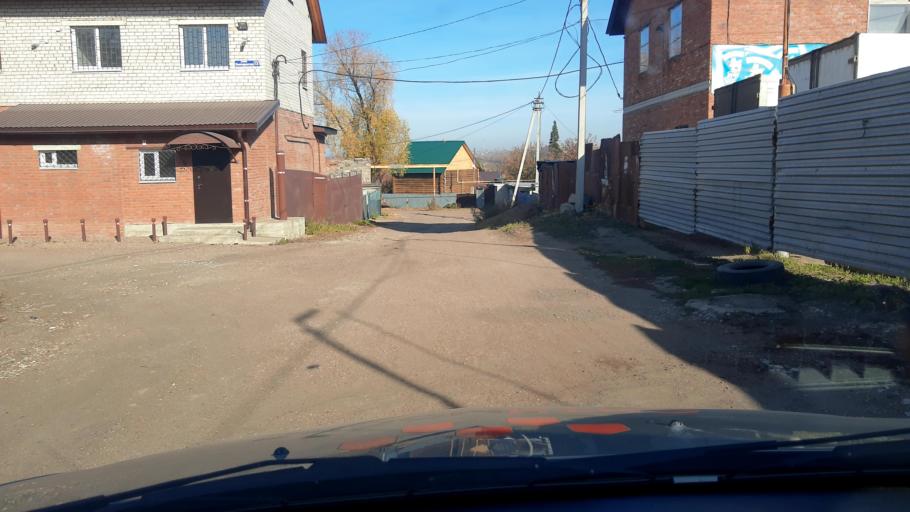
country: RU
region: Bashkortostan
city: Ufa
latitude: 54.8281
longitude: 56.0732
